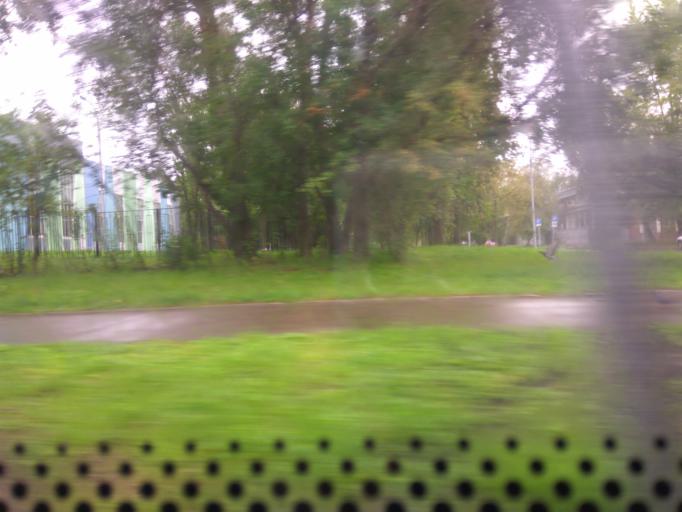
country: RU
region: Moskovskaya
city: Bogorodskoye
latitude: 55.7865
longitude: 37.7302
